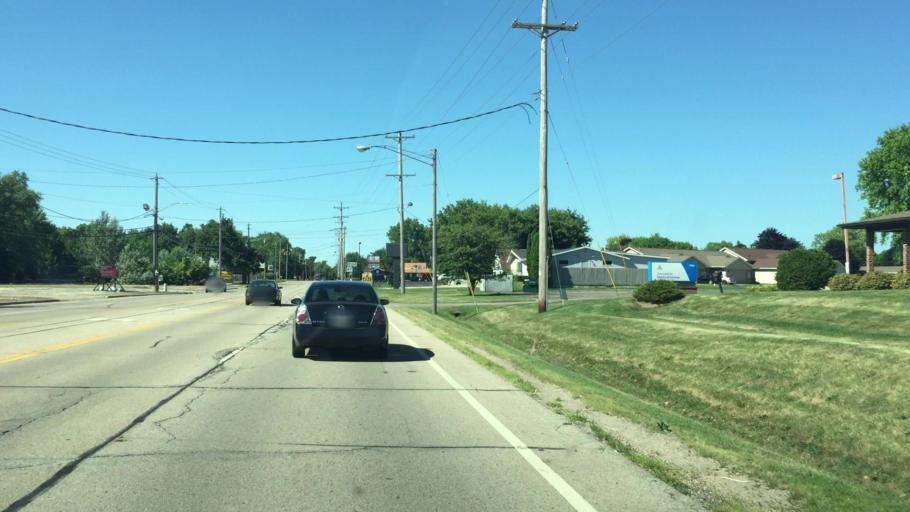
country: US
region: Wisconsin
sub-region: Winnebago County
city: Menasha
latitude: 44.2221
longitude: -88.4279
